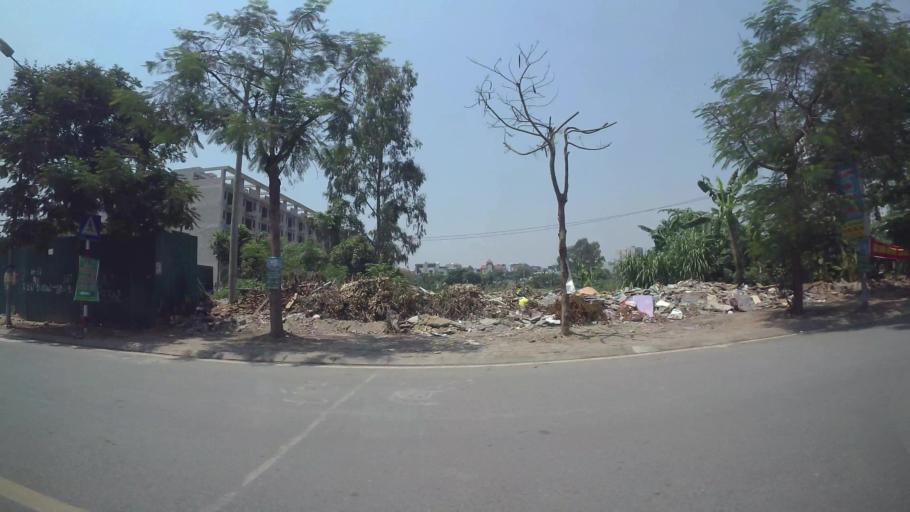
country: VN
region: Ha Noi
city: Hoan Kiem
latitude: 21.0385
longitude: 105.8799
